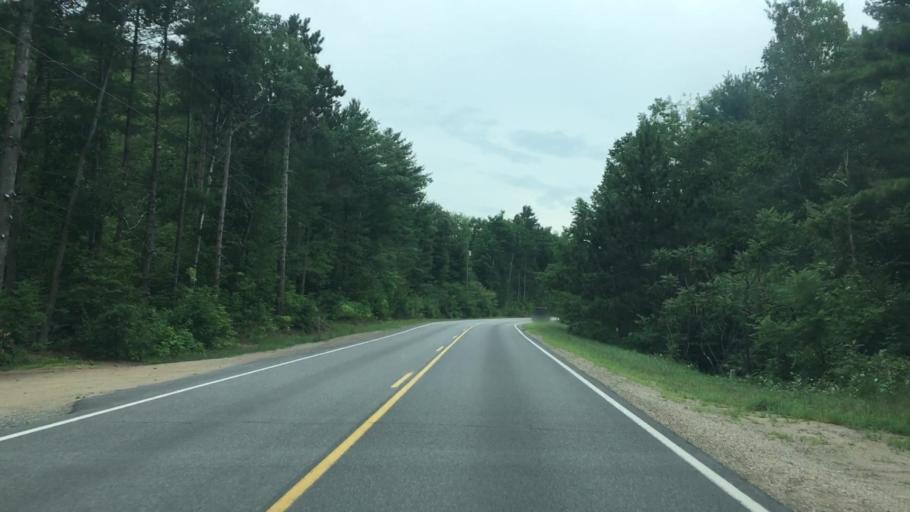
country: US
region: New York
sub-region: Clinton County
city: Peru
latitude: 44.5084
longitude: -73.5839
